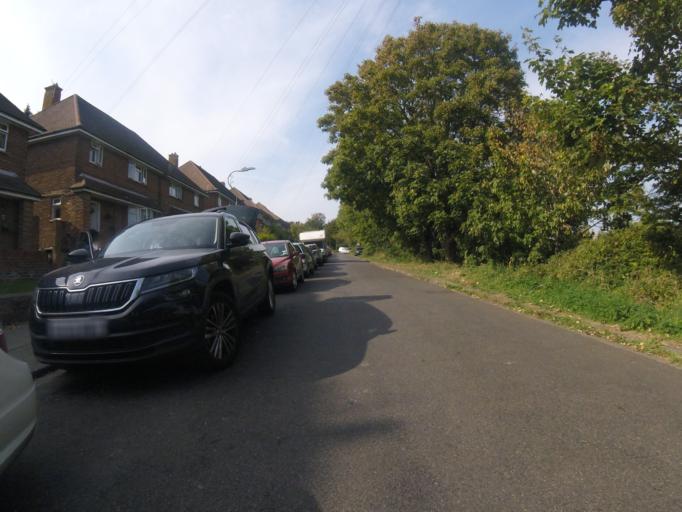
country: GB
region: England
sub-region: East Sussex
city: Portslade
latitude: 50.8525
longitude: -0.1882
